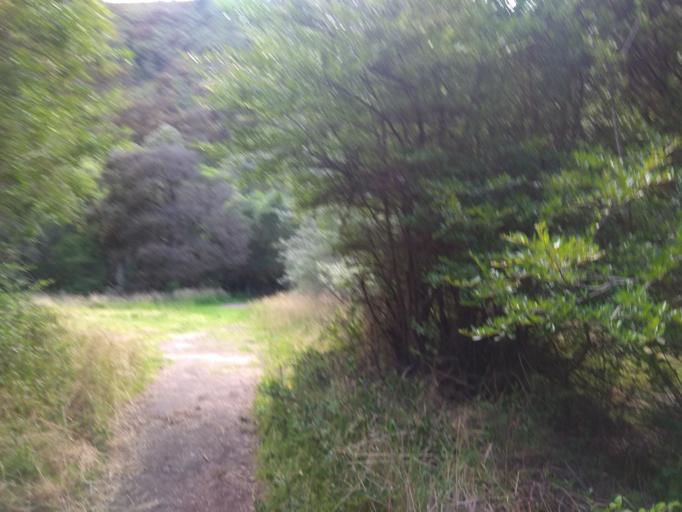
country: CR
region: Cartago
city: Cot
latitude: 9.9649
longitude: -83.8702
